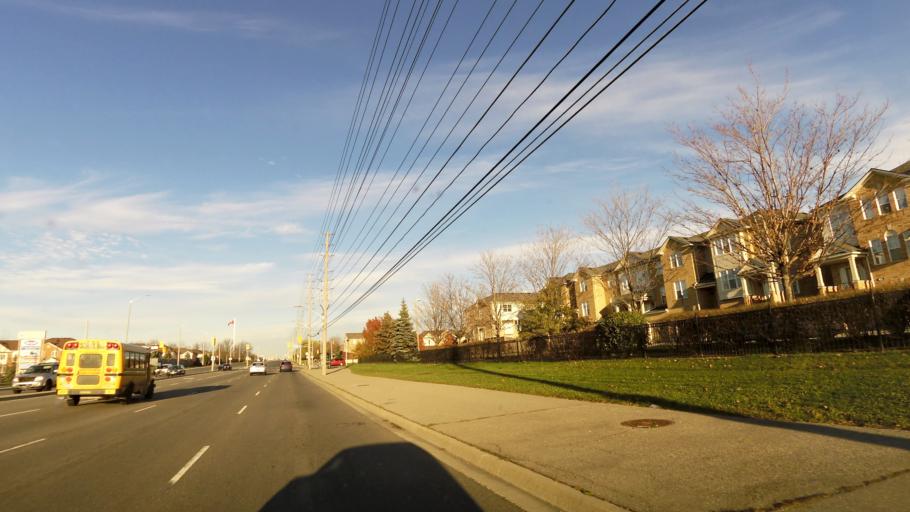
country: CA
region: Ontario
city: Mississauga
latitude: 43.5994
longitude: -79.7098
